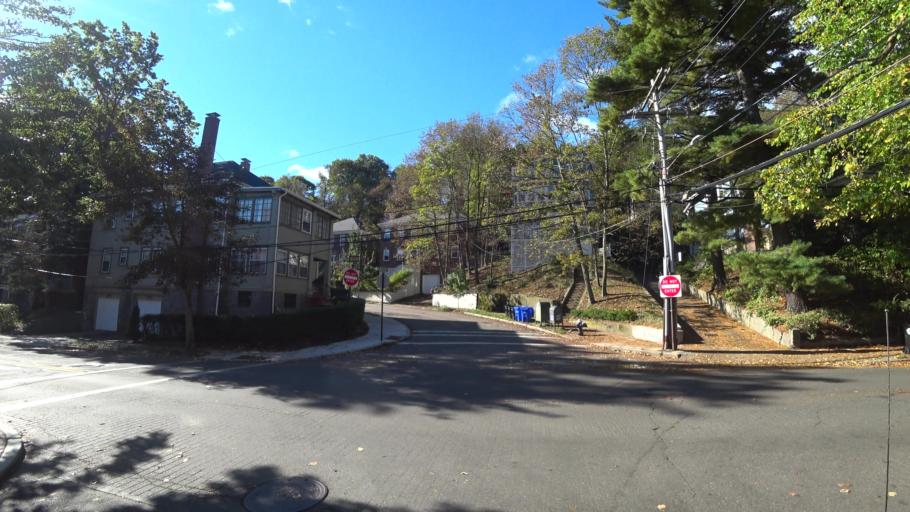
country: US
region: Massachusetts
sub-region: Norfolk County
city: Brookline
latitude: 42.3438
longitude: -71.1287
